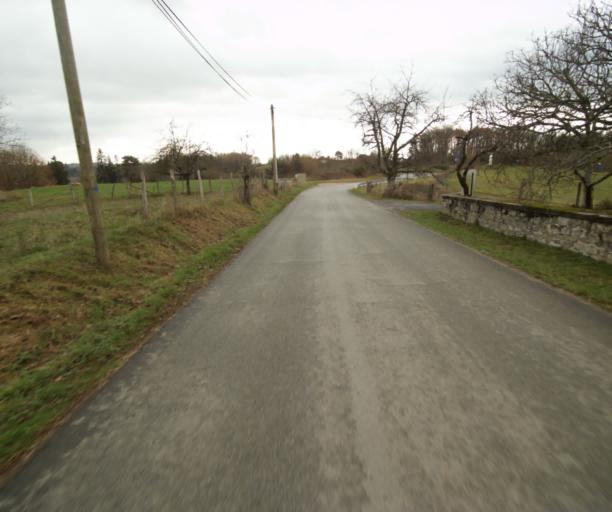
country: FR
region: Limousin
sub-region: Departement de la Correze
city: Saint-Mexant
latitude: 45.2806
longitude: 1.6211
